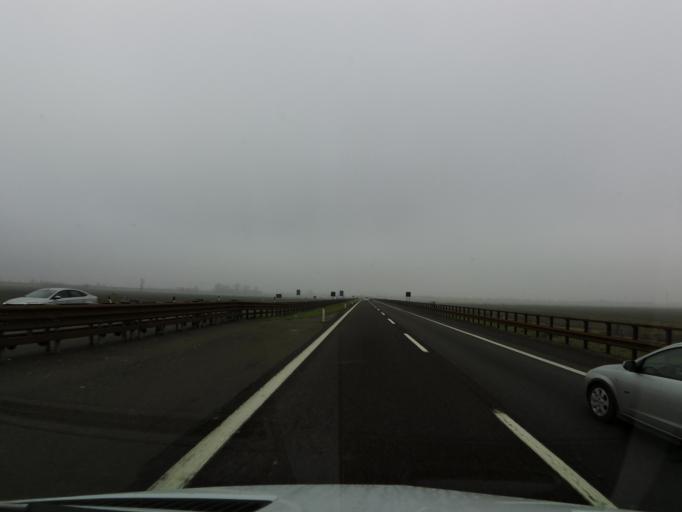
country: IT
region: Emilia-Romagna
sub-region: Provincia di Reggio Emilia
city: Rolo
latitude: 44.8568
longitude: 10.8517
